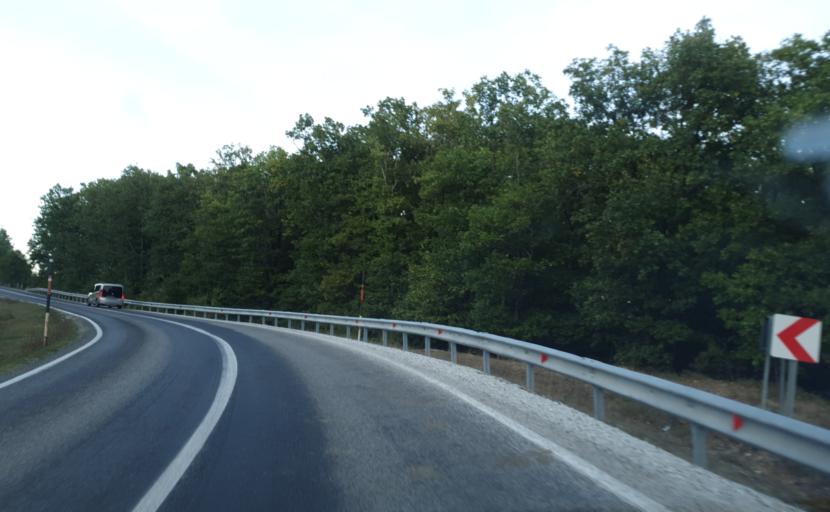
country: TR
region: Kirklareli
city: Igneada
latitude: 41.8595
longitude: 27.8132
